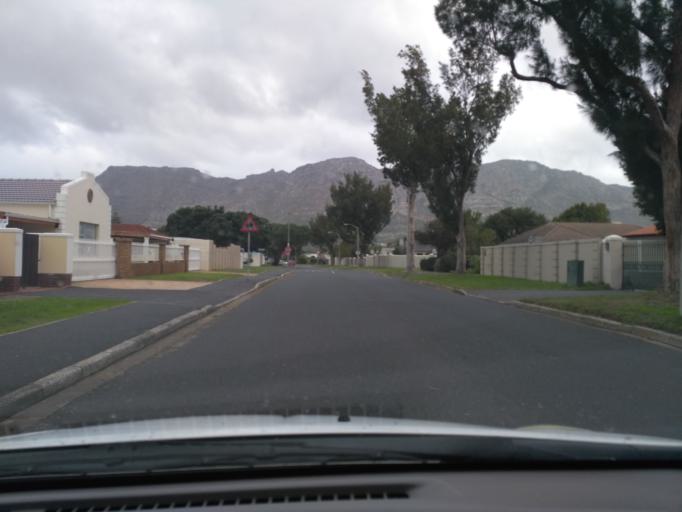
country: ZA
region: Western Cape
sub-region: City of Cape Town
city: Bergvliet
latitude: -34.0679
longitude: 18.4542
